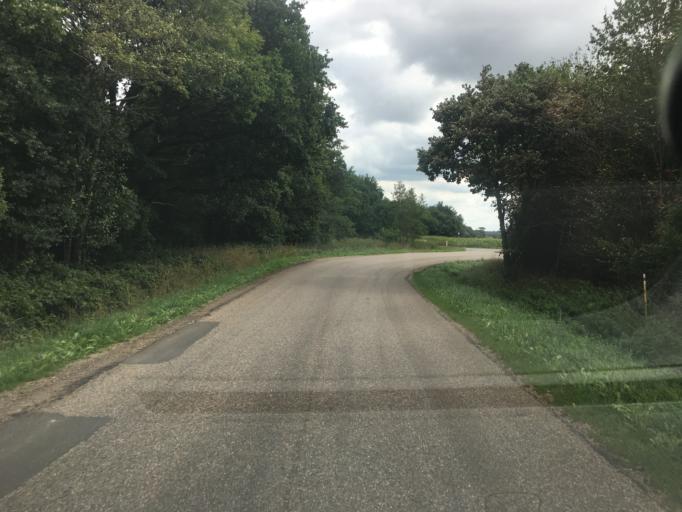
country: DK
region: South Denmark
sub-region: Tonder Kommune
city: Toftlund
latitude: 55.1159
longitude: 9.0387
